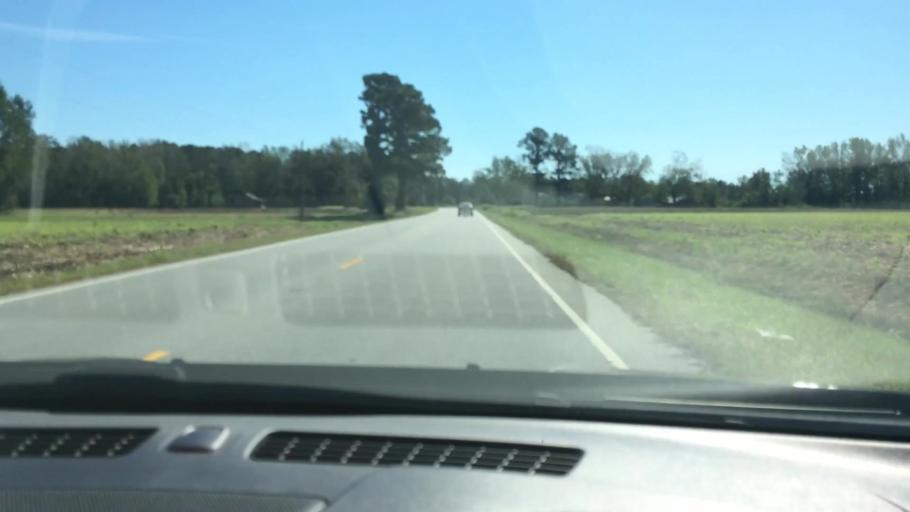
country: US
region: North Carolina
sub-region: Pitt County
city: Grifton
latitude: 35.3582
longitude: -77.3424
